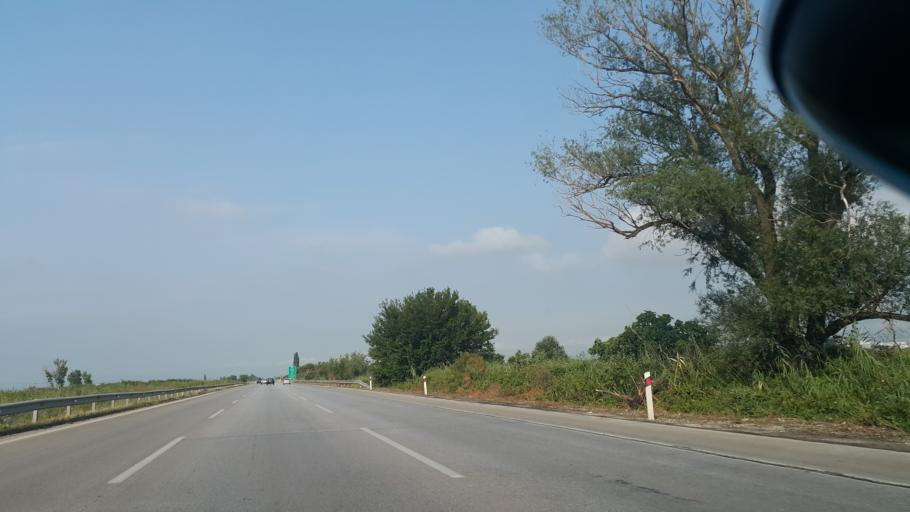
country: GR
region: Central Macedonia
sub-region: Nomos Thessalonikis
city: Chalastra
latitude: 40.6288
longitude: 22.7713
